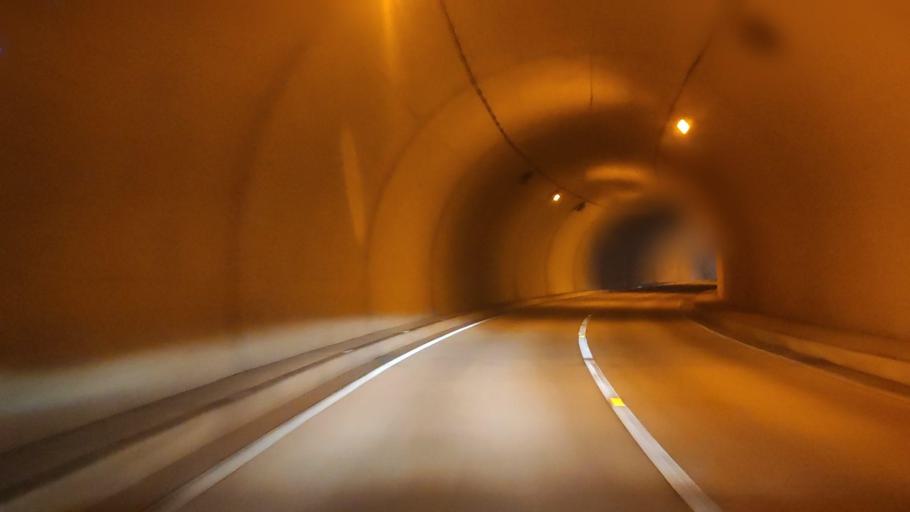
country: JP
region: Nagasaki
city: Shimabara
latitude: 32.7619
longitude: 130.2773
